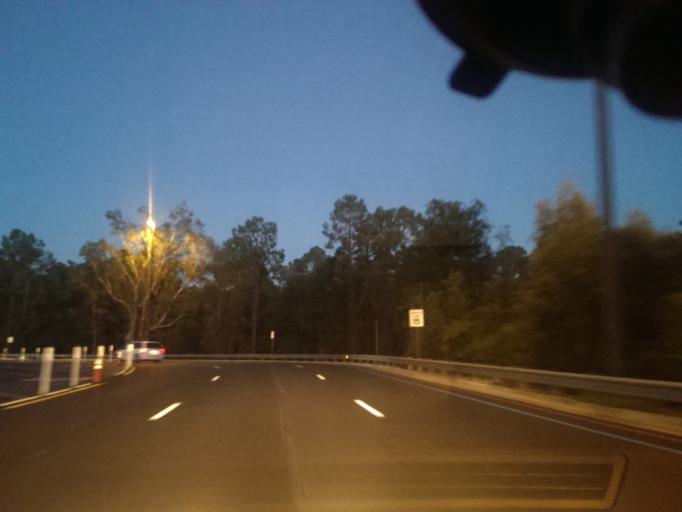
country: US
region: Florida
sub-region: Osceola County
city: Celebration
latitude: 28.3565
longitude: -81.5537
